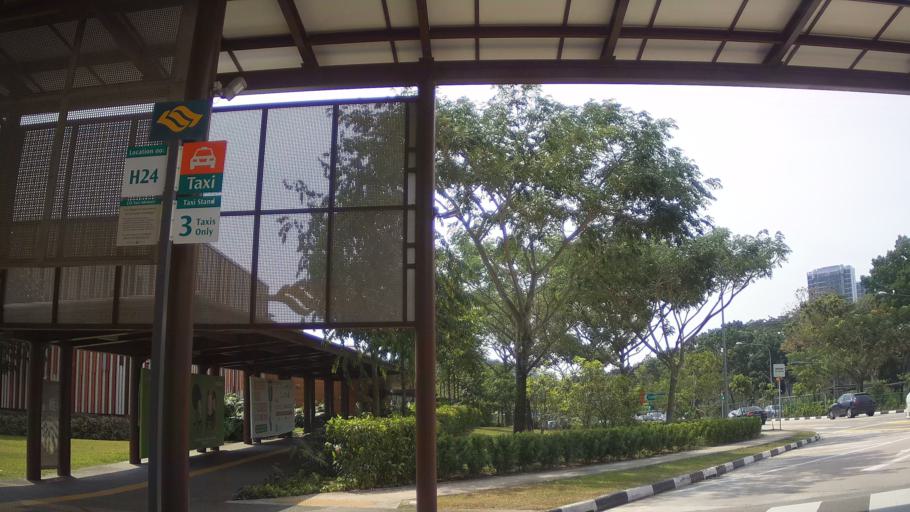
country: MY
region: Johor
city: Johor Bahru
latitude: 1.3702
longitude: 103.7641
